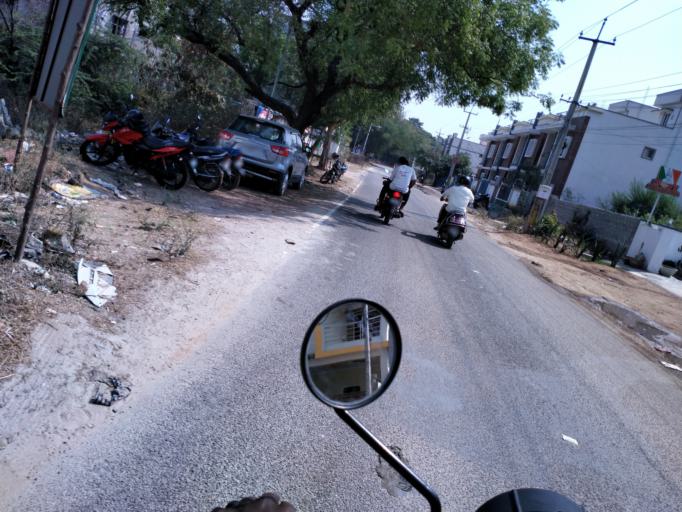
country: IN
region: Telangana
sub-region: Rangareddi
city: Secunderabad
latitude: 17.5018
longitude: 78.5496
